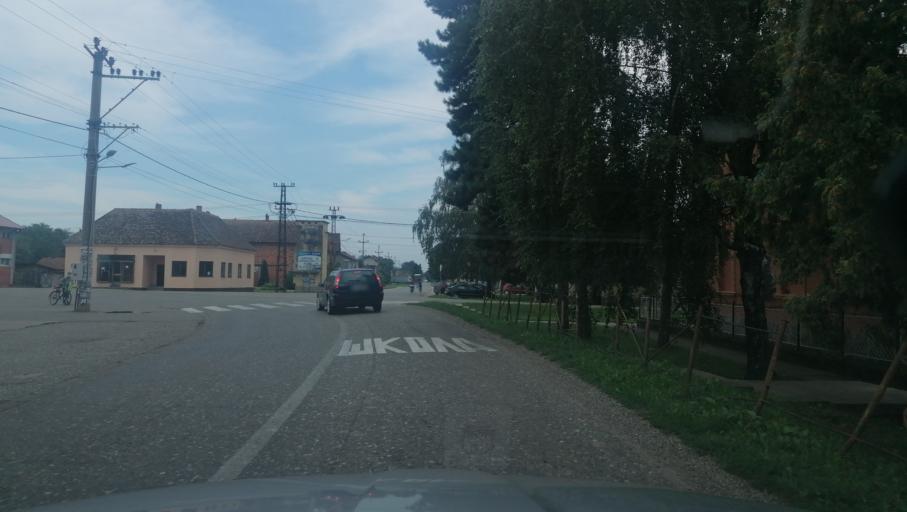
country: RS
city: Klenje
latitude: 44.8071
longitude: 19.4336
